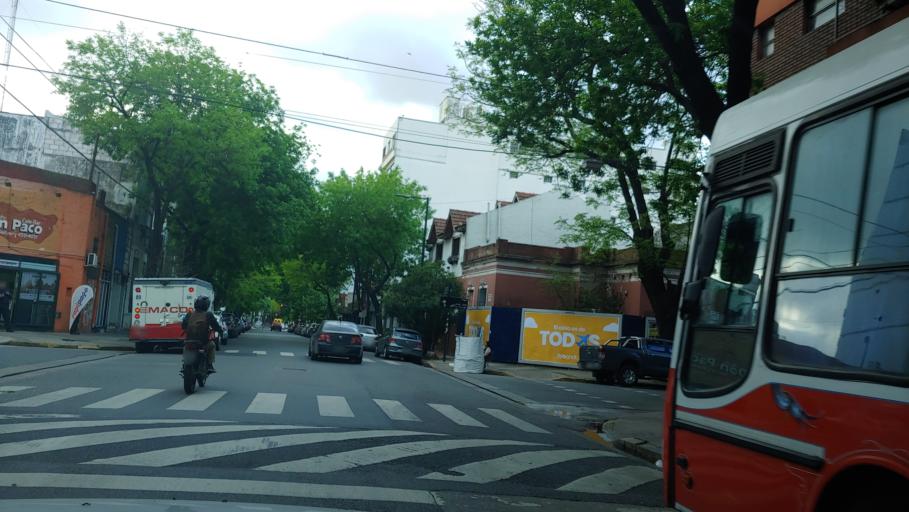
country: AR
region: Buenos Aires F.D.
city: Colegiales
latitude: -34.5761
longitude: -58.4508
